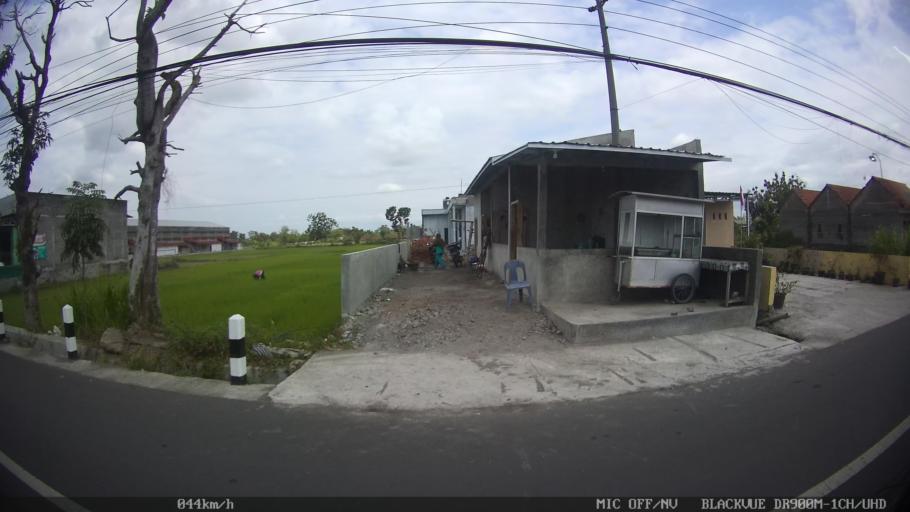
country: ID
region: Central Java
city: Candi Prambanan
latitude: -7.7976
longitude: 110.4828
